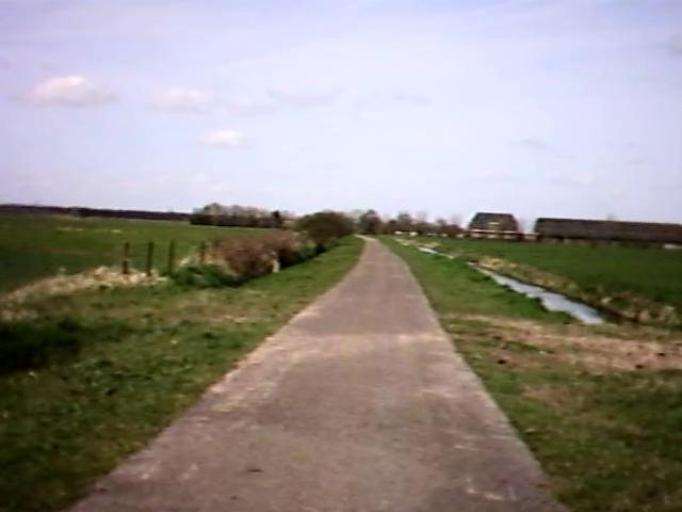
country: NL
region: Utrecht
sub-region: Gemeente De Bilt
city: De Bilt
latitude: 52.1342
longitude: 5.1479
